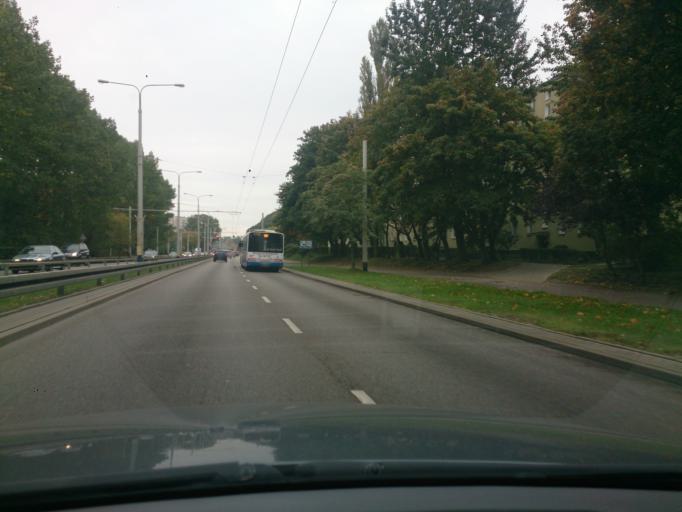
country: PL
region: Pomeranian Voivodeship
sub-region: Gdynia
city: Pogorze
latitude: 54.5396
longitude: 18.4680
